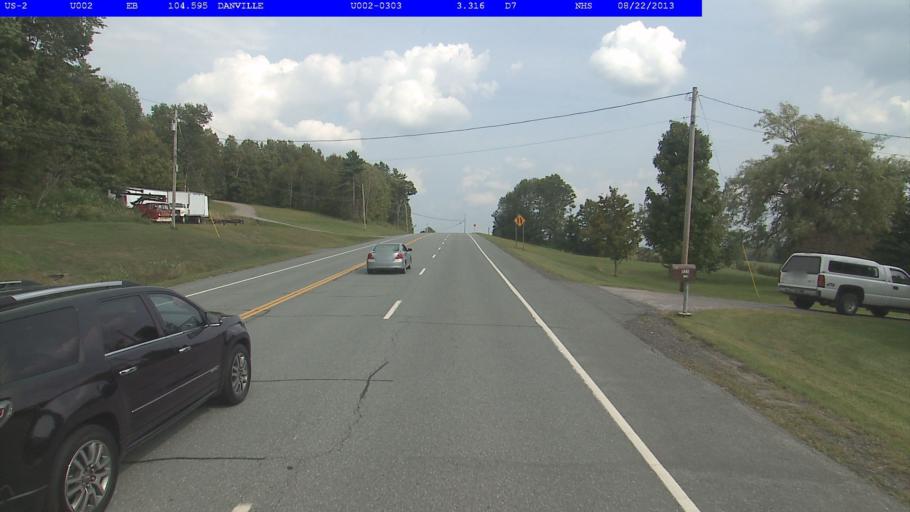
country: US
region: Vermont
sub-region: Caledonia County
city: Saint Johnsbury
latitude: 44.4104
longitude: -72.1628
